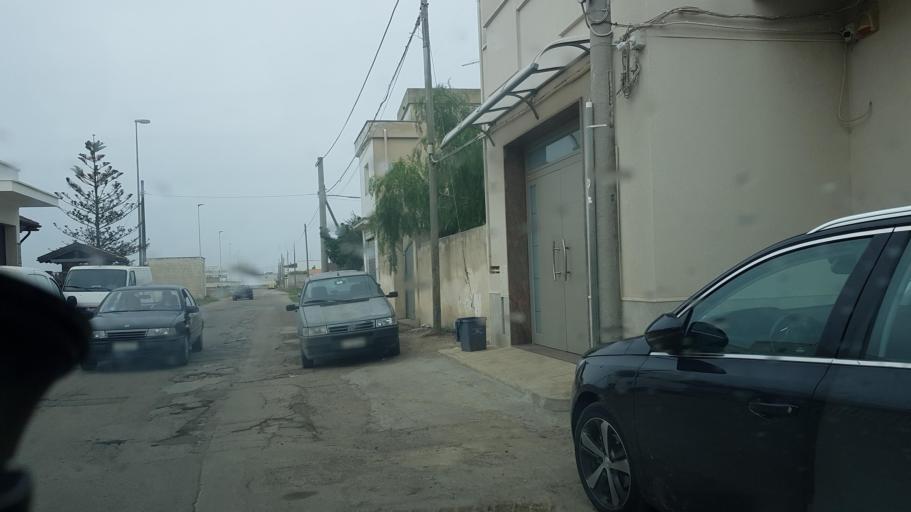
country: IT
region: Apulia
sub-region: Provincia di Lecce
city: Leverano
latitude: 40.2807
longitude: 17.9871
